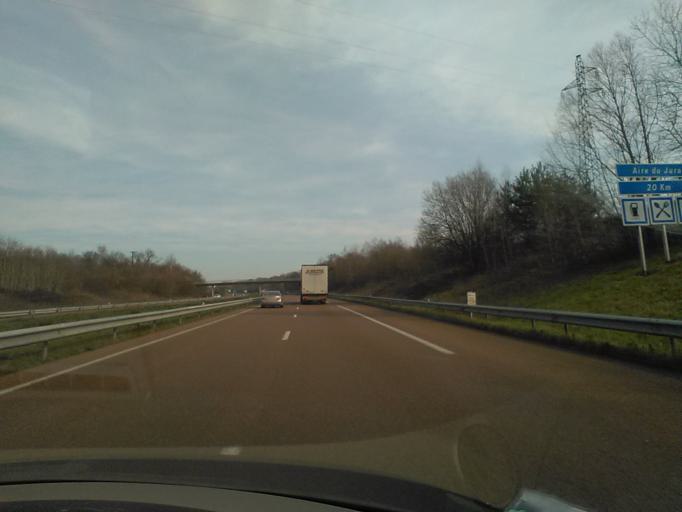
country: FR
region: Bourgogne
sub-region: Departement de Saone-et-Loire
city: Sagy
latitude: 46.6252
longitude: 5.3838
